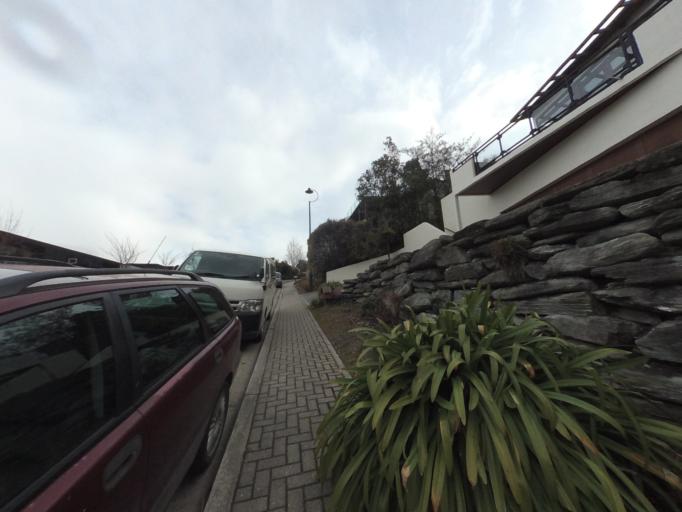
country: NZ
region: Otago
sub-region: Queenstown-Lakes District
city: Queenstown
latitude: -45.0398
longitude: 168.6364
